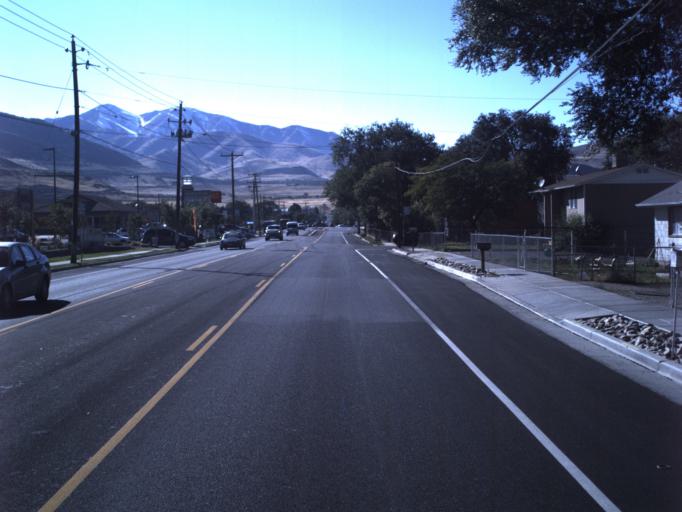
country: US
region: Utah
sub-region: Salt Lake County
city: Magna
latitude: 40.6965
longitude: -112.0873
